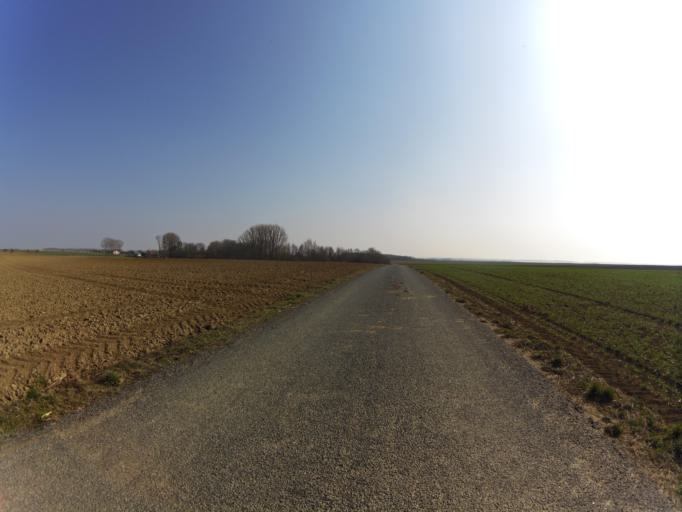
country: DE
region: Bavaria
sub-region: Regierungsbezirk Unterfranken
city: Sulzdorf
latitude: 49.6649
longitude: 9.9176
